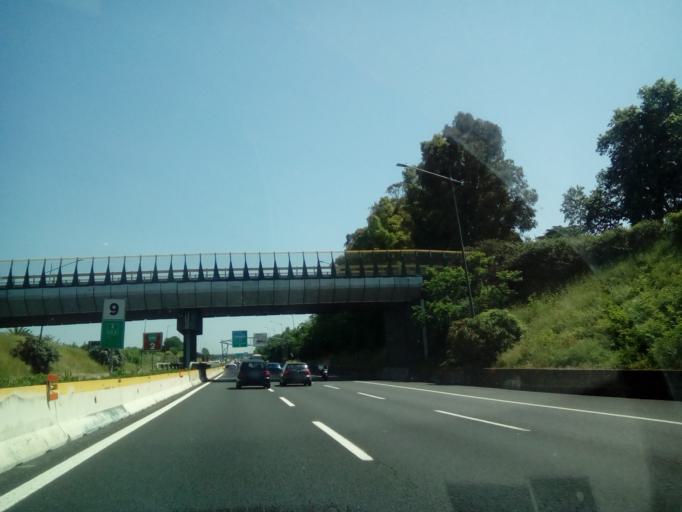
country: IT
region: Latium
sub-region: Citta metropolitana di Roma Capitale
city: Valle Santa
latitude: 41.9613
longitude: 12.3919
